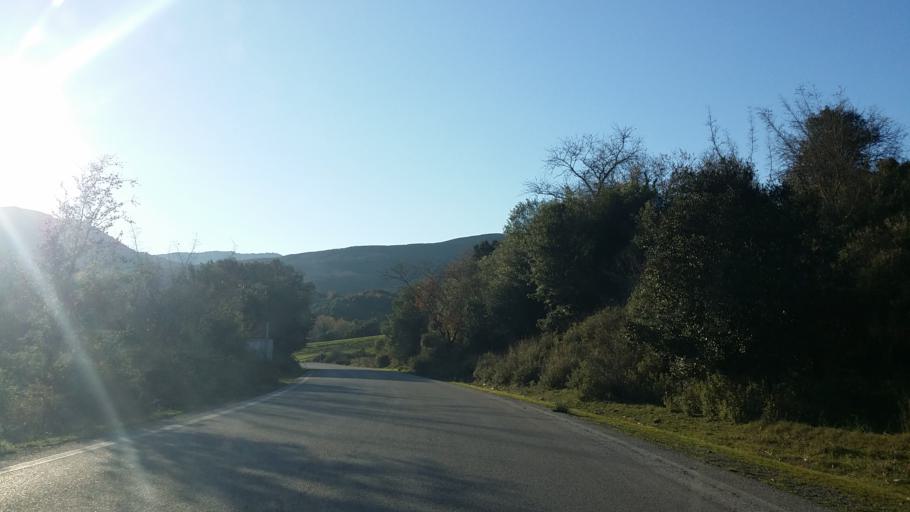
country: GR
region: West Greece
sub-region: Nomos Aitolias kai Akarnanias
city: Sardinia
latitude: 38.8516
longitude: 21.3359
